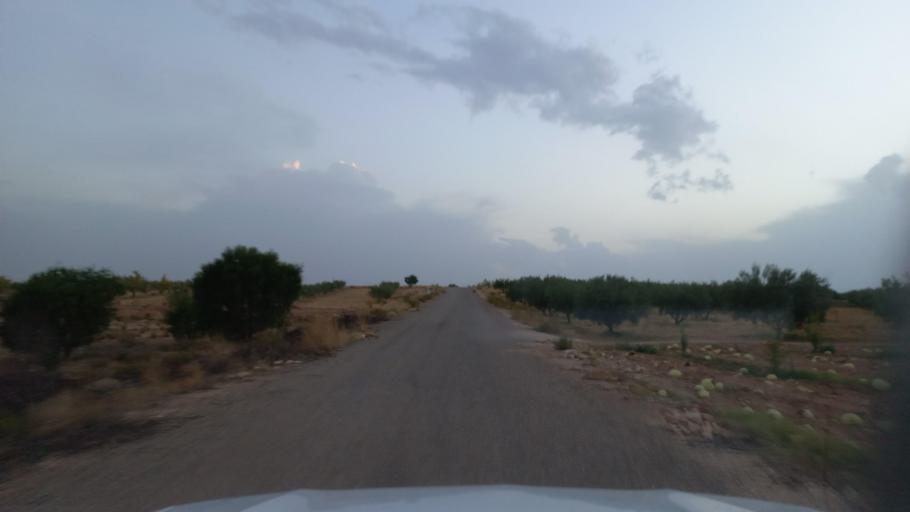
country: TN
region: Al Qasrayn
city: Kasserine
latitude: 35.2703
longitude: 9.0372
